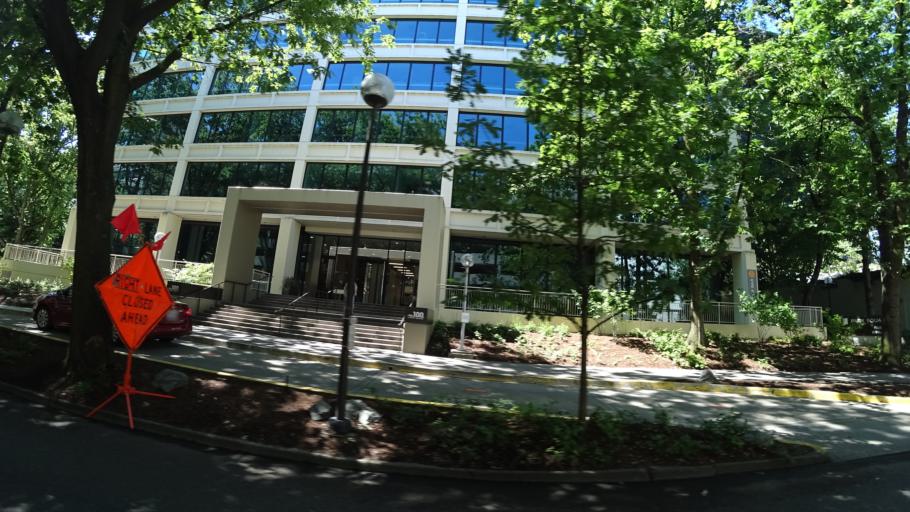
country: US
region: Oregon
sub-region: Multnomah County
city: Portland
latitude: 45.5119
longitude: -122.6777
